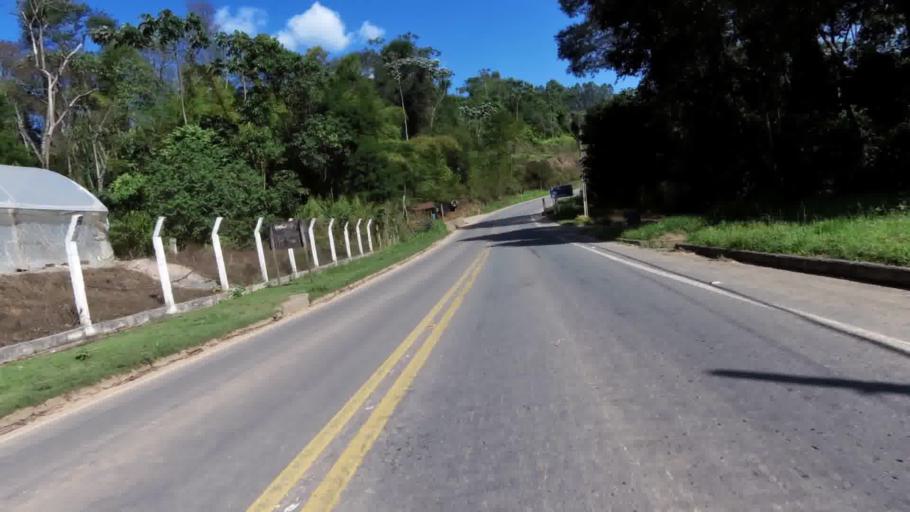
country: BR
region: Espirito Santo
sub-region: Marechal Floriano
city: Marechal Floriano
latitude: -20.4464
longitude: -40.7851
